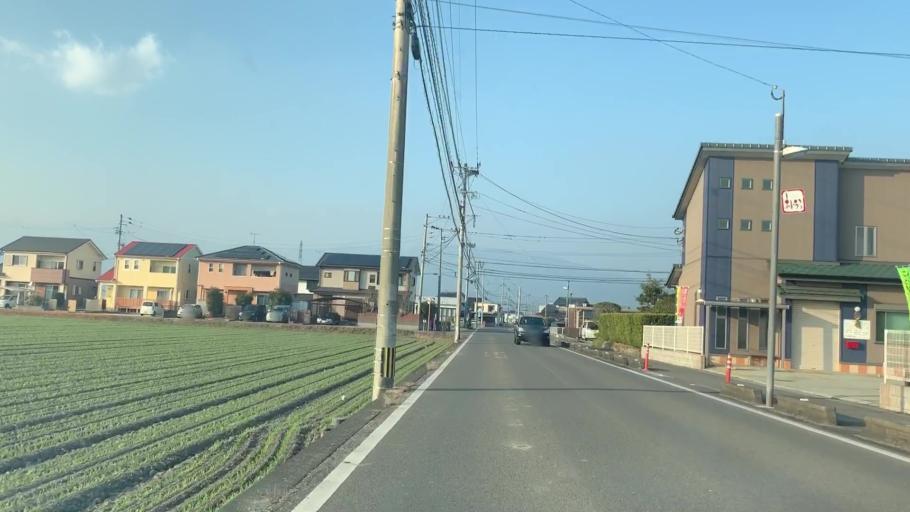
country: JP
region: Saga Prefecture
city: Saga-shi
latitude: 33.2640
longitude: 130.2312
